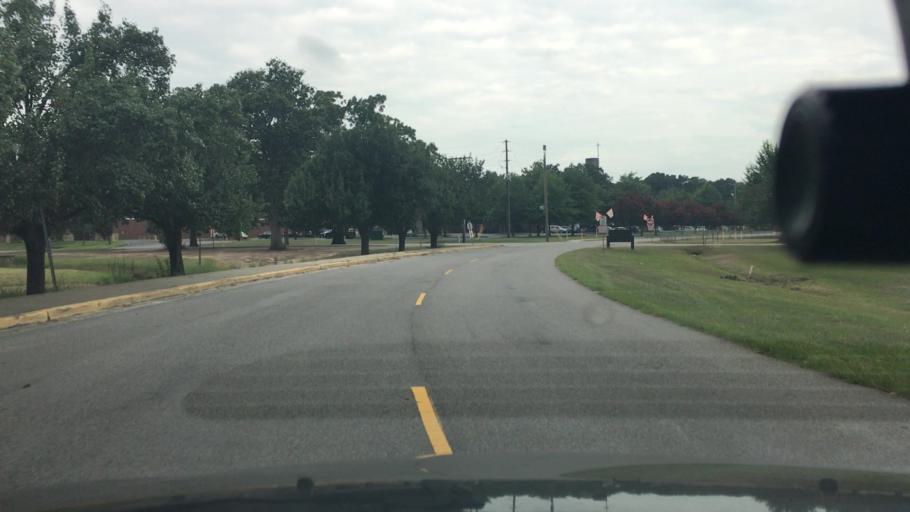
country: US
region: South Carolina
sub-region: Aiken County
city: Aiken
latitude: 33.5228
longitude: -81.7142
